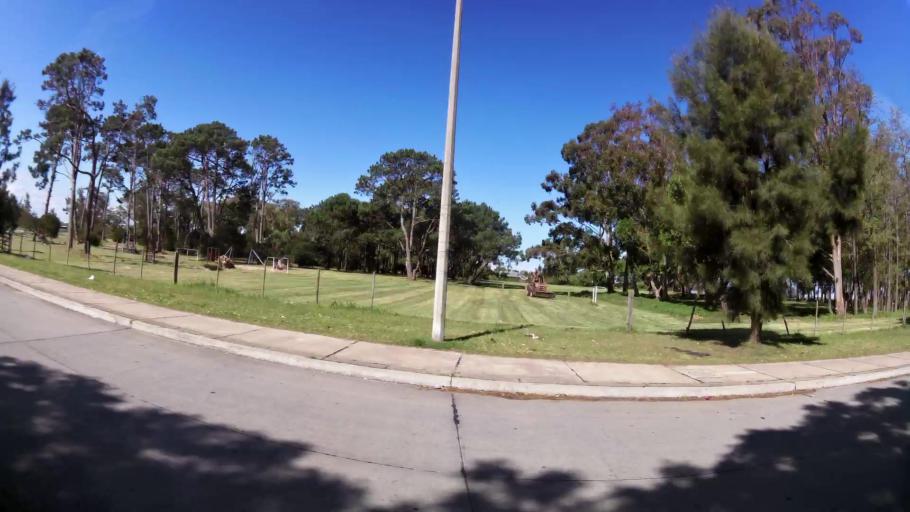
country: UY
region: Canelones
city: Barra de Carrasco
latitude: -34.8779
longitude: -56.0373
